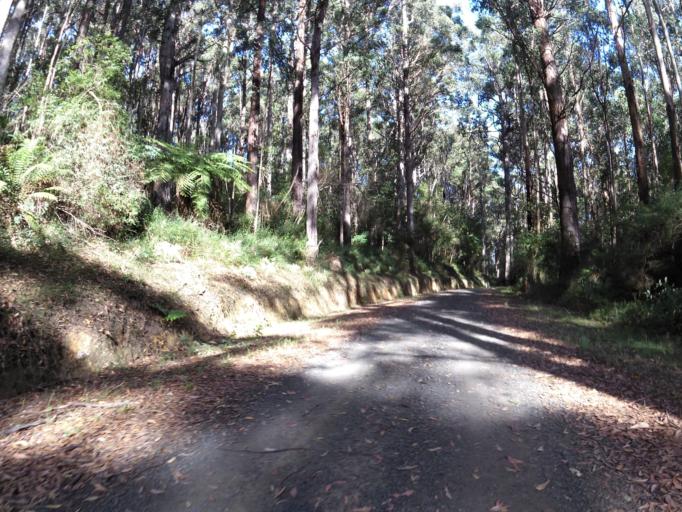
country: AU
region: Victoria
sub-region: Yarra Ranges
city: Millgrove
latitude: -37.8507
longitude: 145.7977
